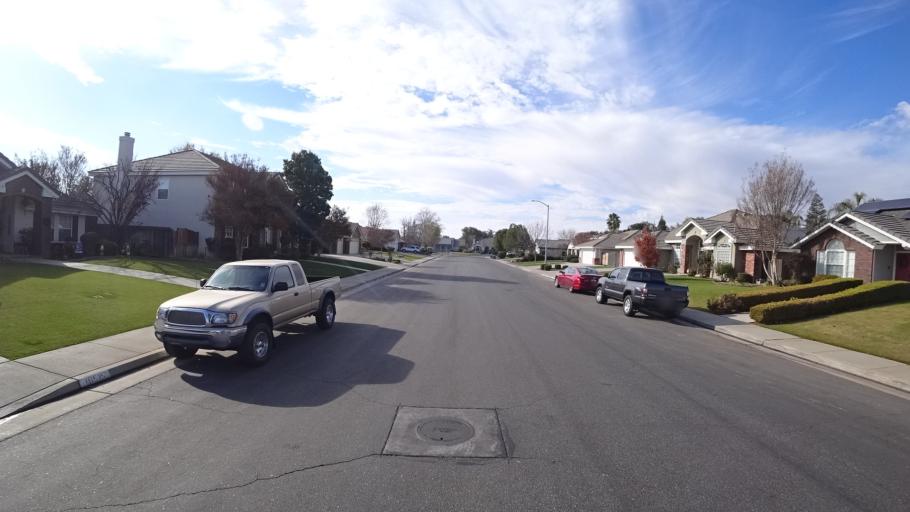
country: US
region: California
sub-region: Kern County
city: Greenacres
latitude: 35.4029
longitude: -119.1200
